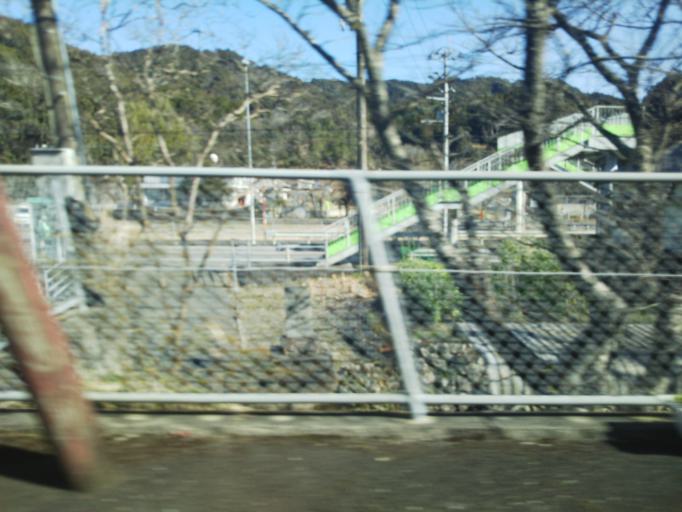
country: JP
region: Kochi
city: Nakamura
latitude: 33.1051
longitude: 133.0987
